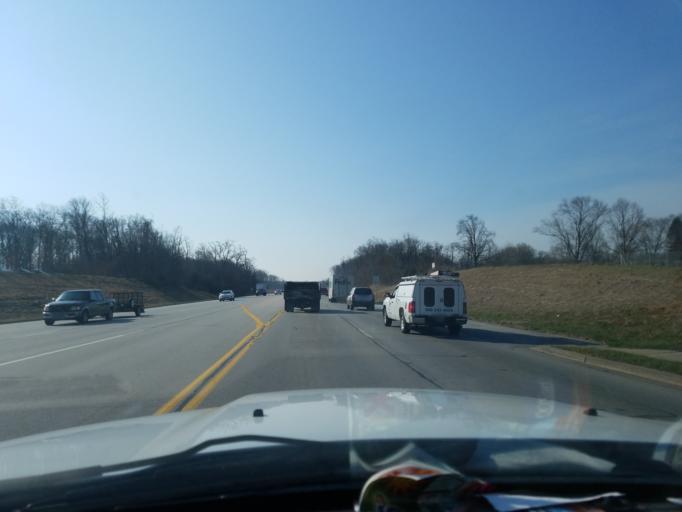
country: US
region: Indiana
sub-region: Monroe County
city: Ellettsville
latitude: 39.2075
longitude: -86.5799
